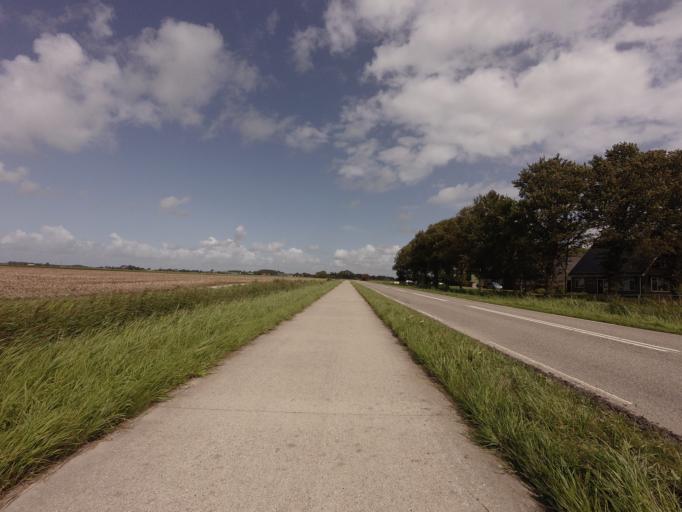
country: NL
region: Friesland
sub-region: Gemeente Harlingen
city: Harlingen
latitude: 53.1397
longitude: 5.4746
